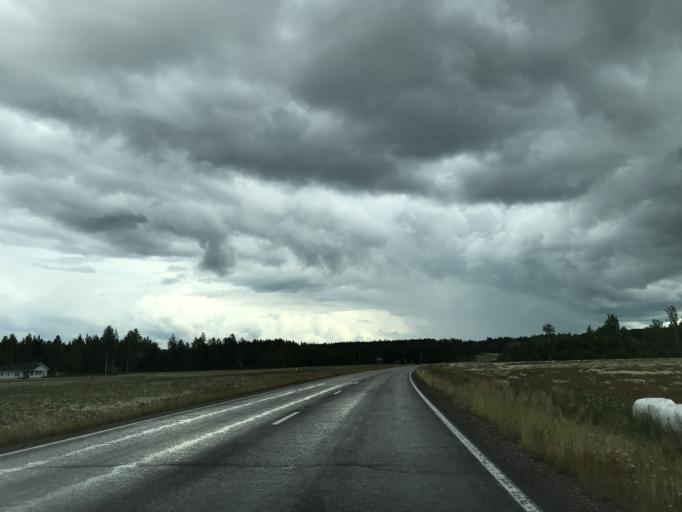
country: FI
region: Uusimaa
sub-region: Porvoo
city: Pukkila
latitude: 60.7748
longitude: 25.5577
